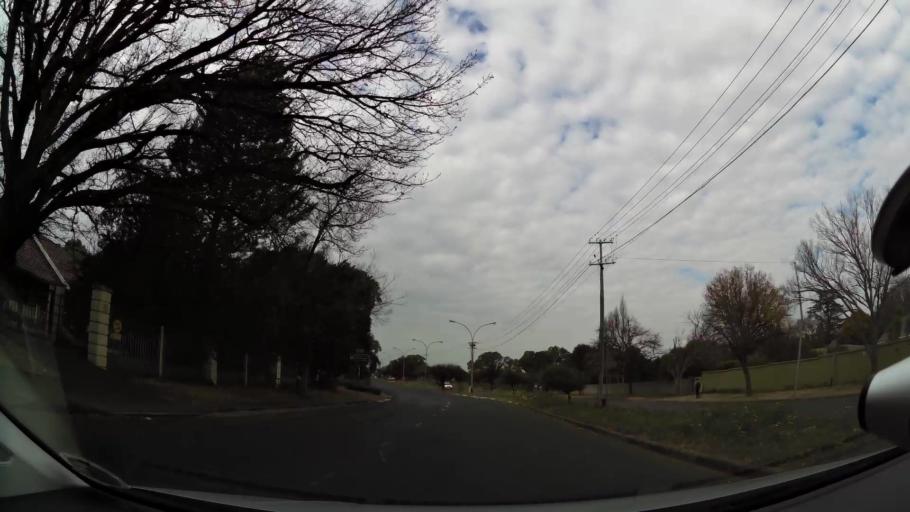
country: ZA
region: Orange Free State
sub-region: Mangaung Metropolitan Municipality
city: Bloemfontein
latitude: -29.0835
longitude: 26.2199
